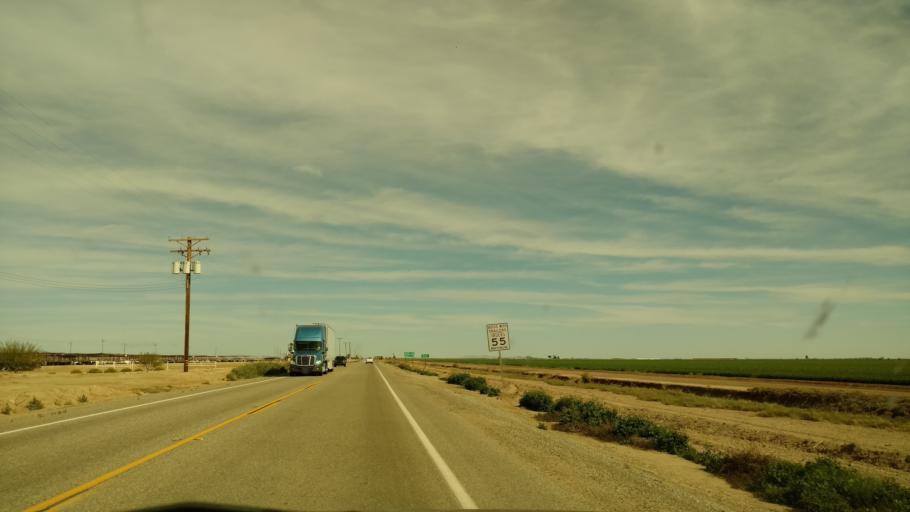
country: US
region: California
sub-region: Imperial County
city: Brawley
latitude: 32.9745
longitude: -115.4028
